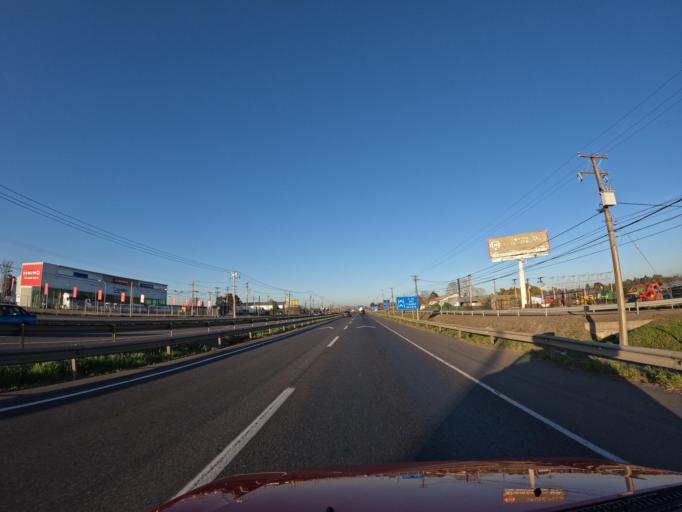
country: CL
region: Biobio
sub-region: Provincia de Nuble
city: Chillan
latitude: -36.6292
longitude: -72.1721
